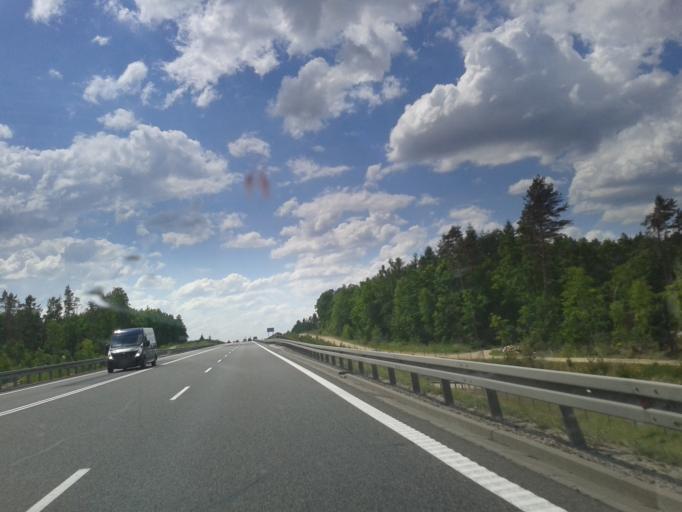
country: PL
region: Pomeranian Voivodeship
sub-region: Powiat chojnicki
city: Chojnice
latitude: 53.7022
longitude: 17.6341
